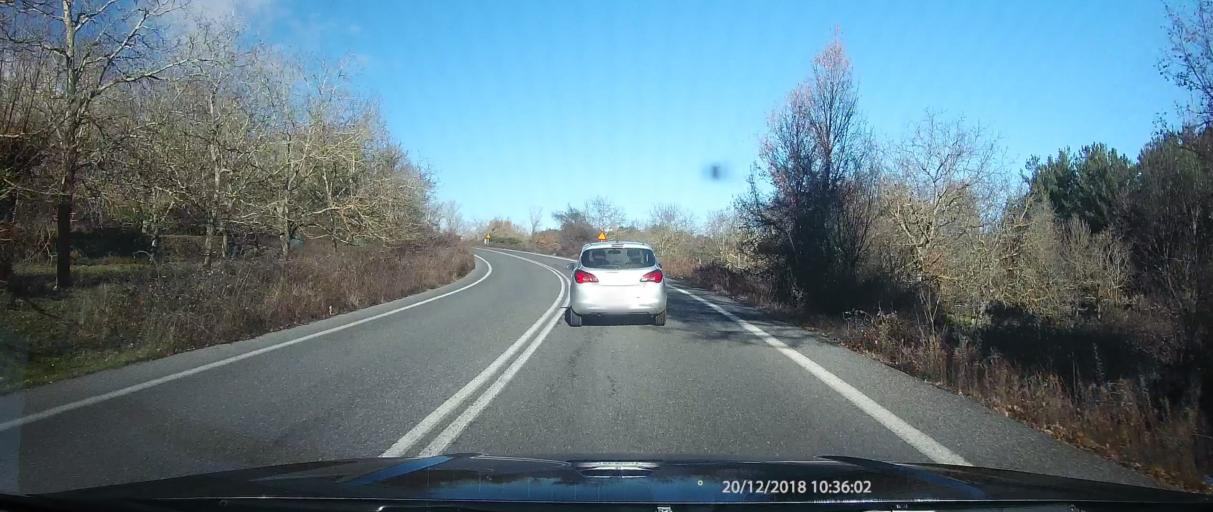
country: GR
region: Peloponnese
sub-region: Nomos Lakonias
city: Kariai
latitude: 37.3616
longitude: 22.4046
